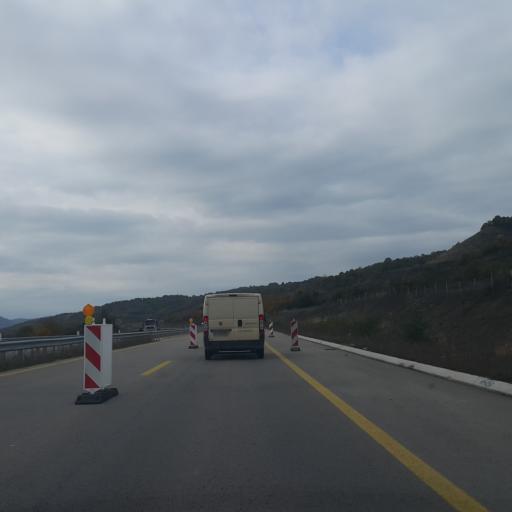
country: RS
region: Central Serbia
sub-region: Pirotski Okrug
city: Bela Palanka
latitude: 43.2360
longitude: 22.3497
